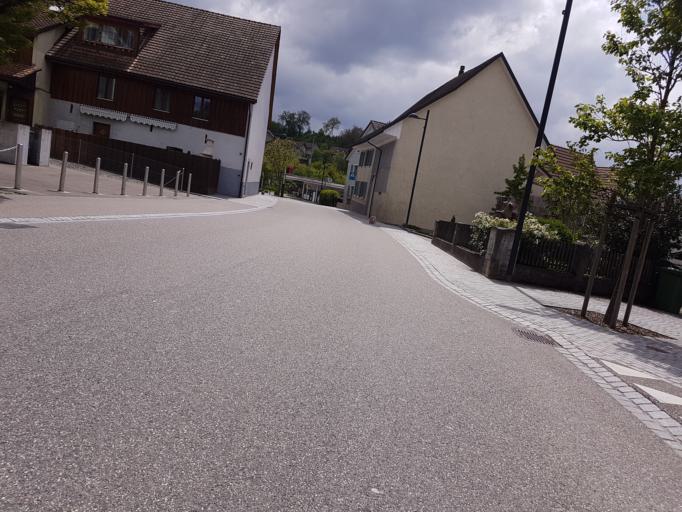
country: CH
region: Aargau
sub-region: Bezirk Zurzach
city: Klingnau
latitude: 47.5703
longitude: 8.2563
